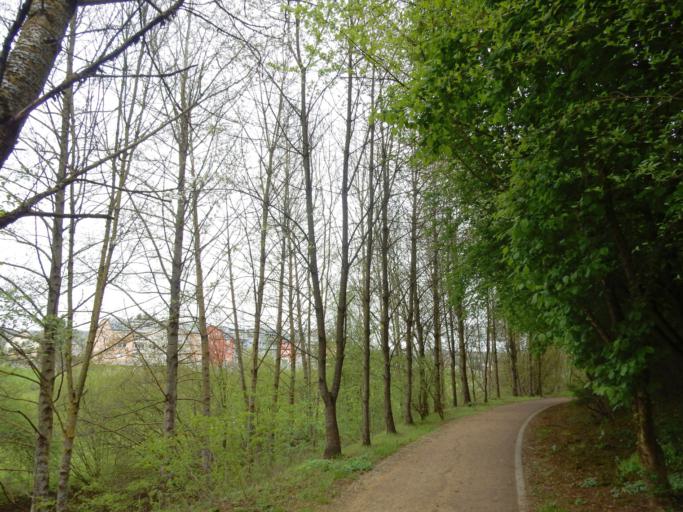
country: LU
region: Luxembourg
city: Lamadelaine
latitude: 49.5572
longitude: 5.8625
